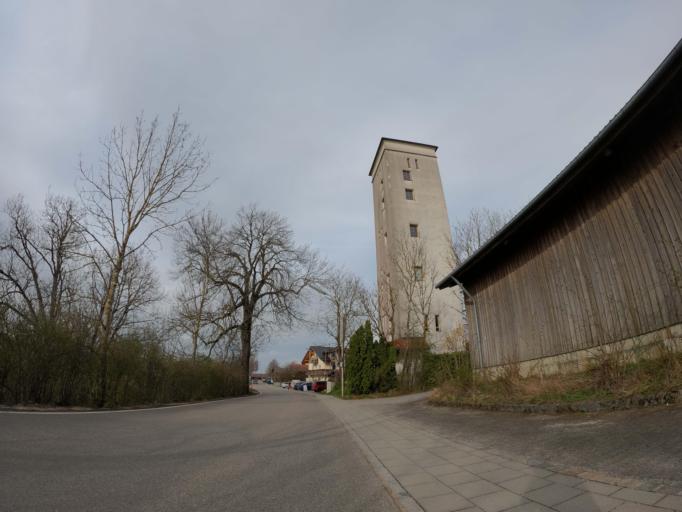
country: DE
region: Bavaria
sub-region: Upper Bavaria
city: Taufkirchen
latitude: 48.0365
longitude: 11.6182
